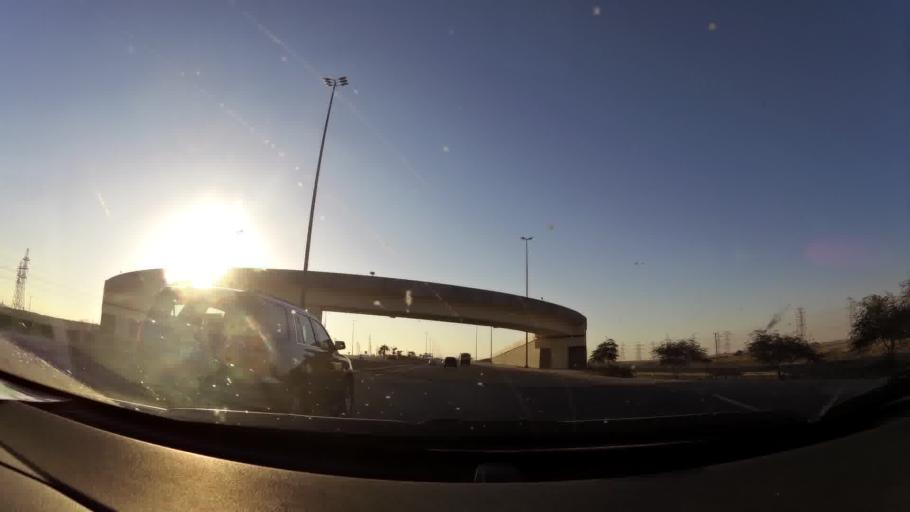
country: KW
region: Al Ahmadi
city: Al Fahahil
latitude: 28.8860
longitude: 48.2261
